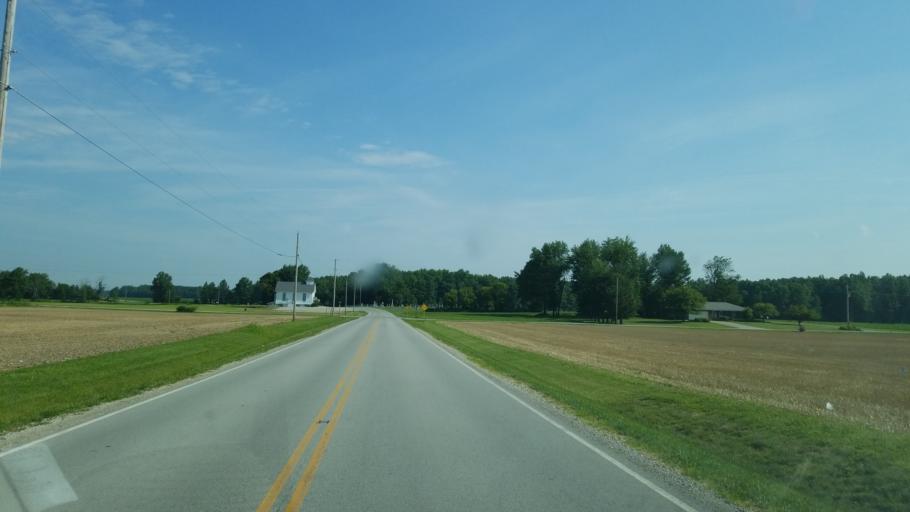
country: US
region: Ohio
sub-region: Huron County
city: Willard
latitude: 41.0069
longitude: -82.8526
